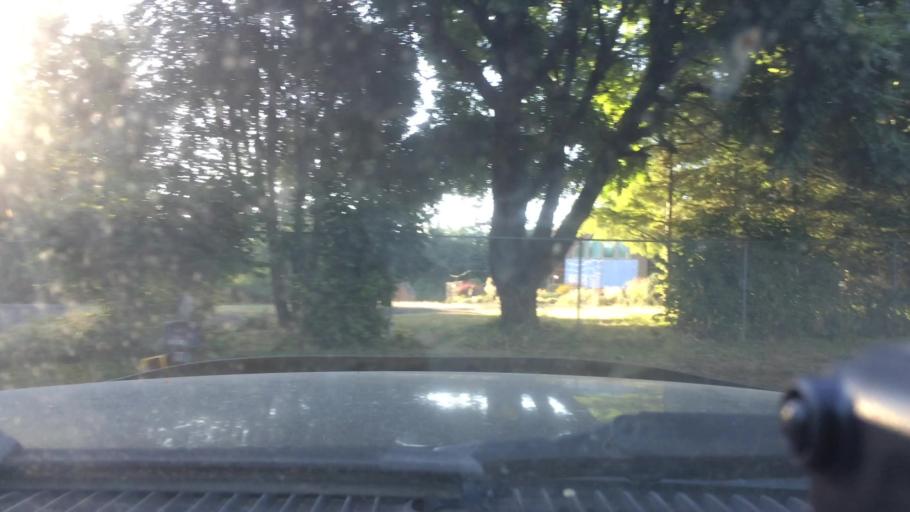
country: US
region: Oregon
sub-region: Yamhill County
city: Newberg
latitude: 45.3763
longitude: -122.9755
